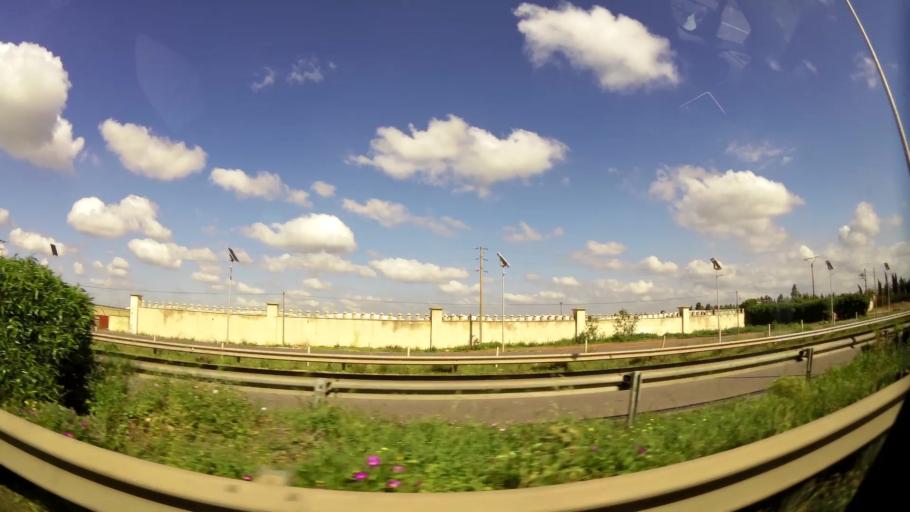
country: MA
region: Chaouia-Ouardigha
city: Nouaseur
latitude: 33.4139
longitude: -7.6265
